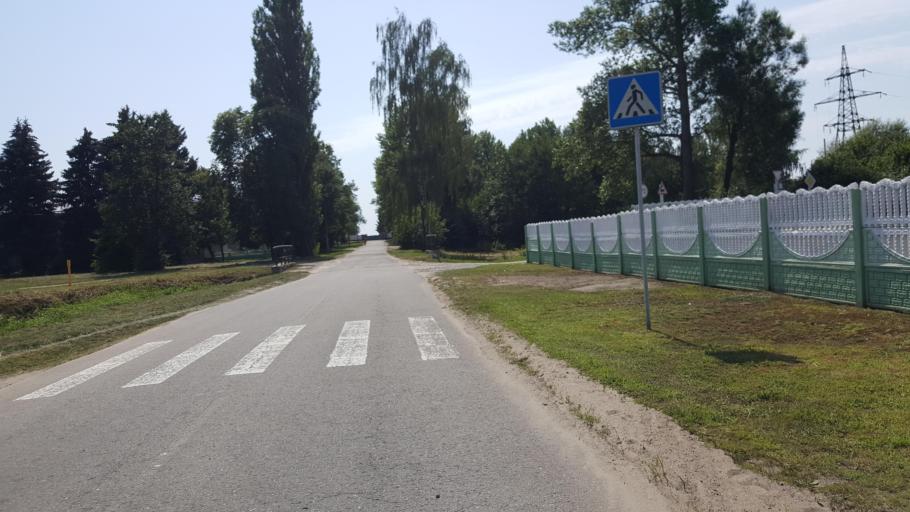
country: BY
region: Brest
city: Zhabinka
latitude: 52.1915
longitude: 24.0175
